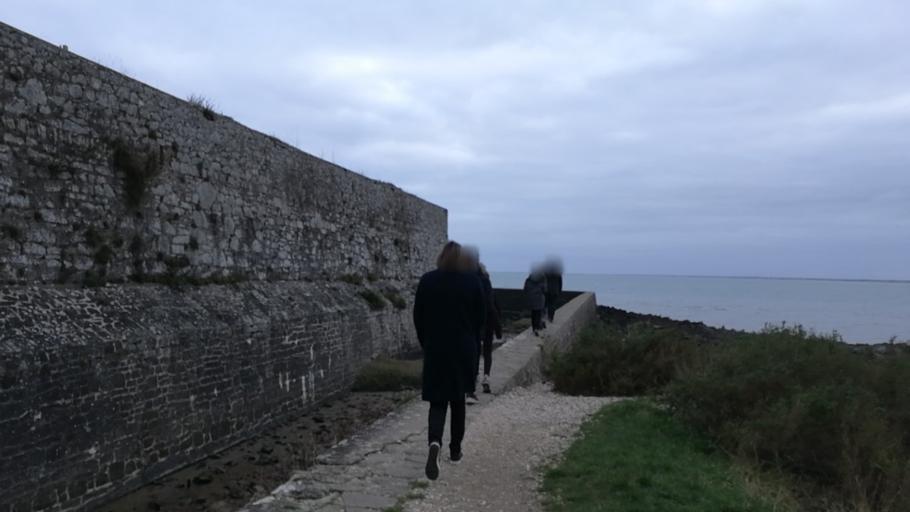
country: FR
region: Lower Normandy
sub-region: Departement de la Manche
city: Saint-Vaast-la-Hougue
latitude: 49.5712
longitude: -1.2735
